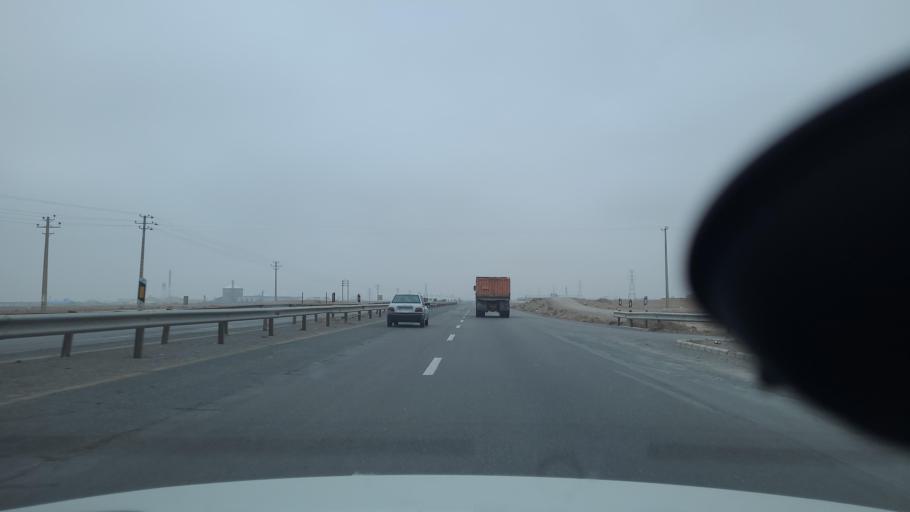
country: IR
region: Razavi Khorasan
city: Fariman
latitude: 35.9507
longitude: 59.7489
